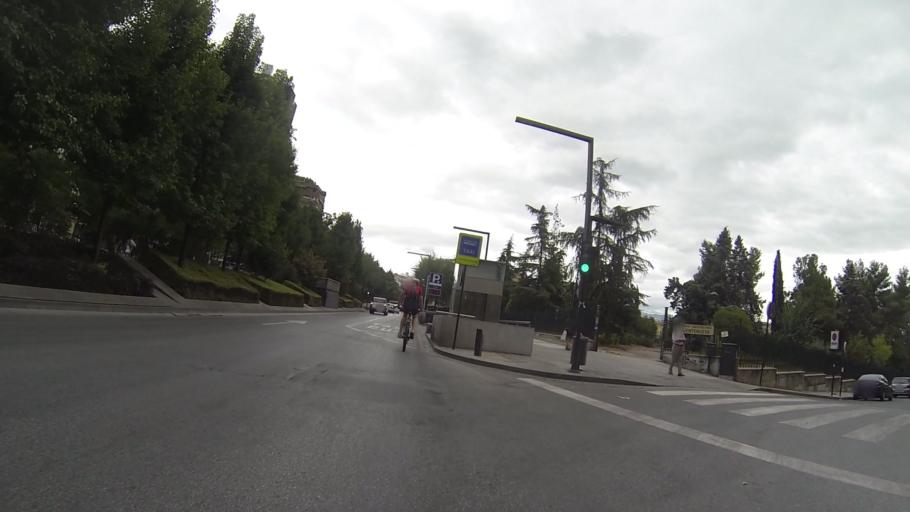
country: ES
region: Andalusia
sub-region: Provincia de Granada
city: Granada
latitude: 37.1850
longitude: -3.6061
